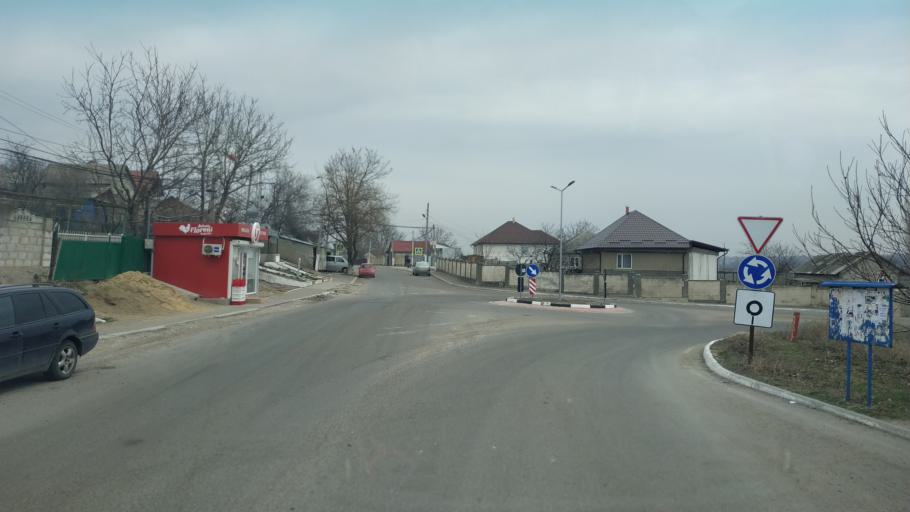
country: MD
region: Chisinau
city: Singera
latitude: 46.9327
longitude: 28.9852
